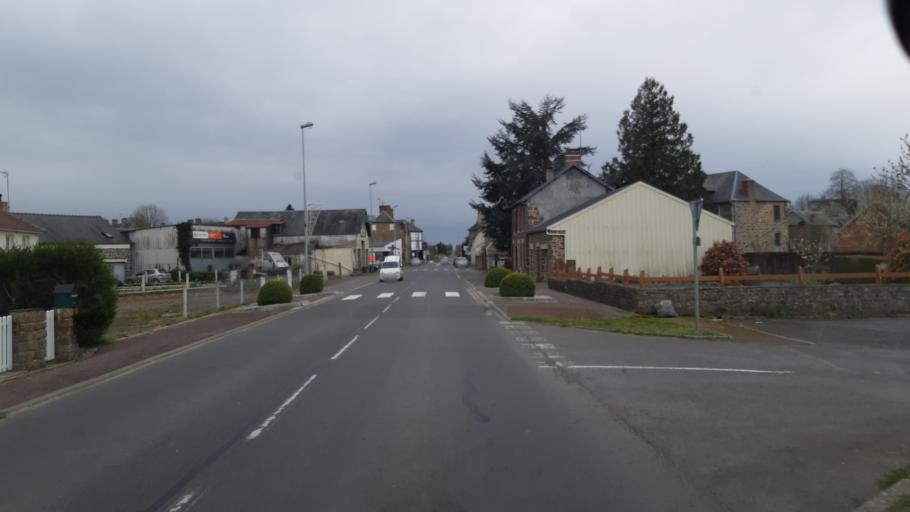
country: FR
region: Lower Normandy
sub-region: Departement de la Manche
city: Hambye
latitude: 48.9485
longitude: -1.2616
